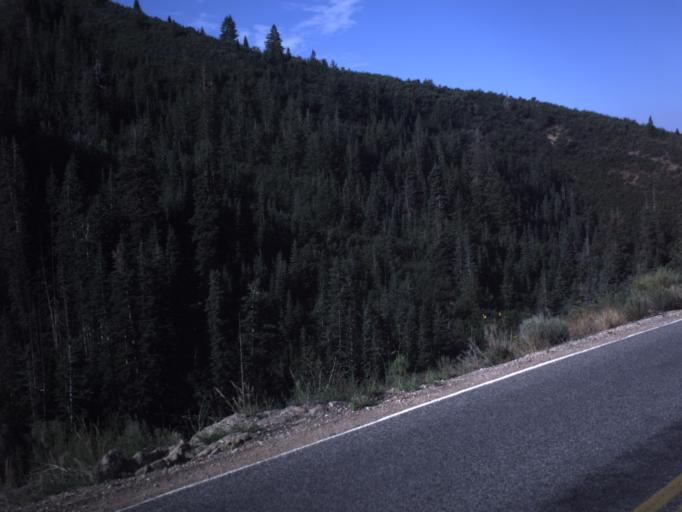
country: US
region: Utah
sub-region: Sanpete County
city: Fairview
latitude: 39.6486
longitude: -111.3960
